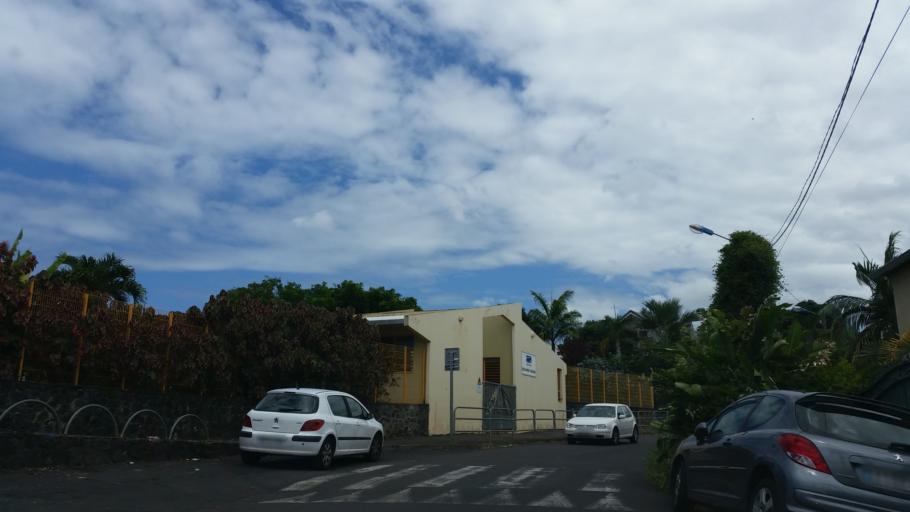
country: RE
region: Reunion
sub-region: Reunion
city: Sainte-Marie
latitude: -20.9257
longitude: 55.5189
